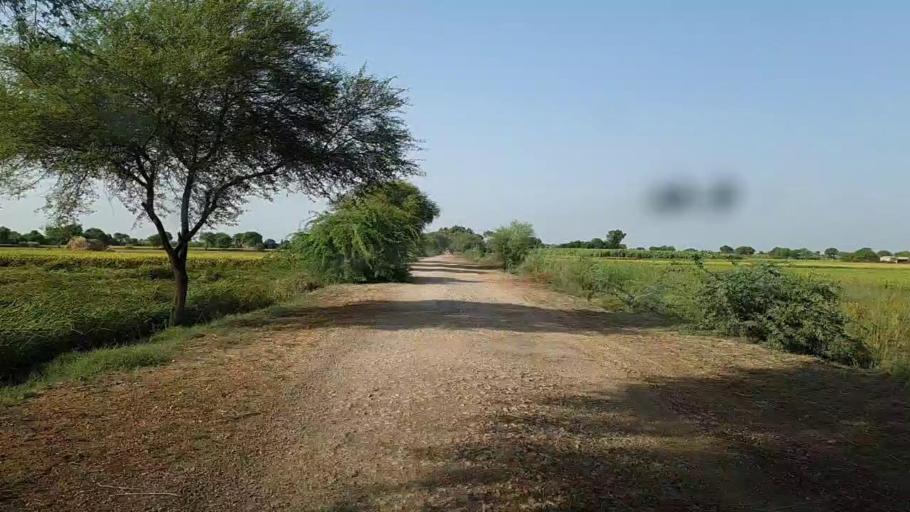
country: PK
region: Sindh
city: Bulri
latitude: 24.7819
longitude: 68.4355
